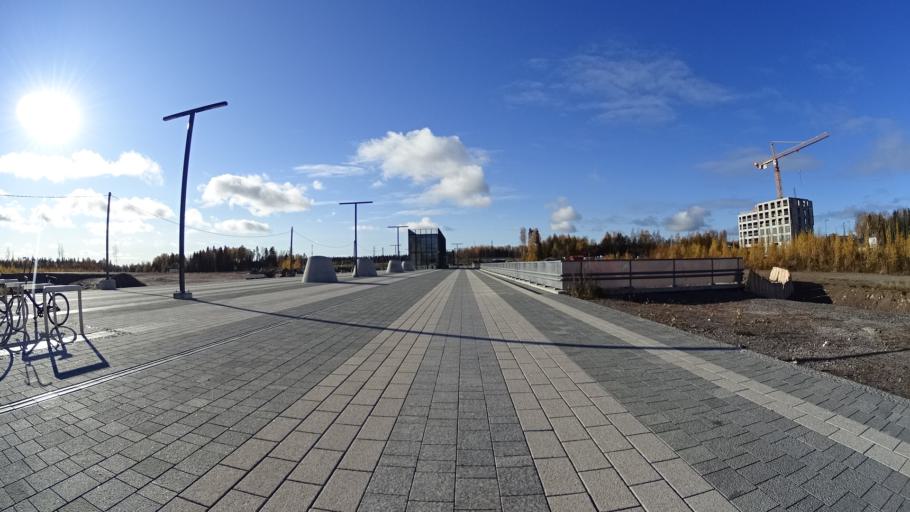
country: FI
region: Uusimaa
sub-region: Helsinki
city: Kilo
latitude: 60.3153
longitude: 24.8484
